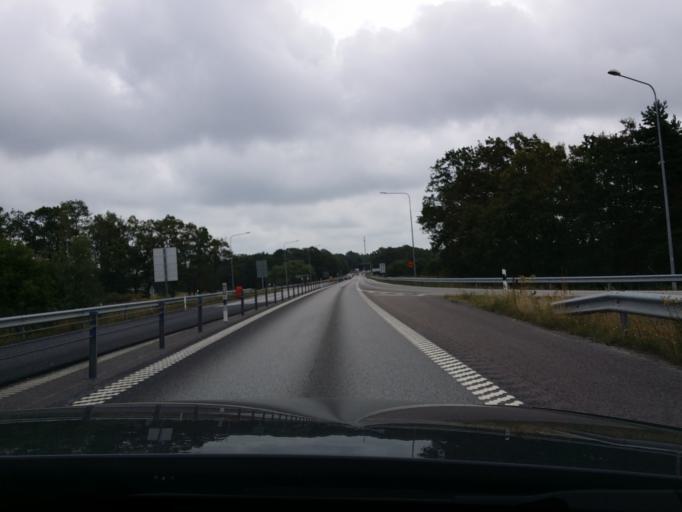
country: SE
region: Blekinge
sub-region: Karlshamns Kommun
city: Morrum
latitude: 56.1766
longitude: 14.7276
